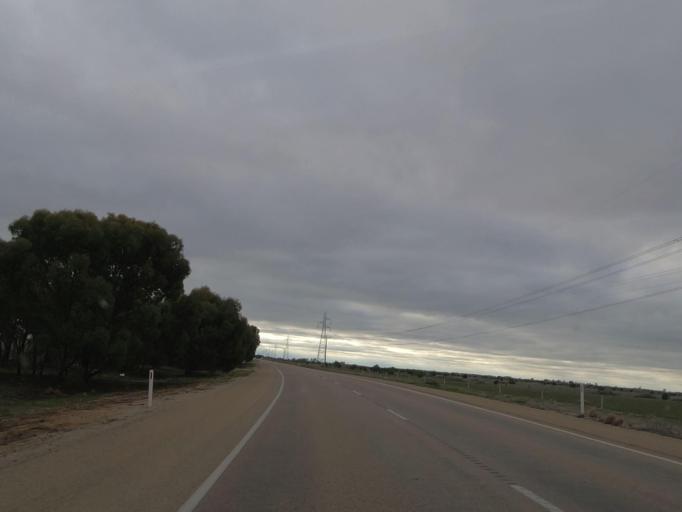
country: AU
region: Victoria
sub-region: Swan Hill
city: Swan Hill
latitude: -35.9046
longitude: 143.9471
